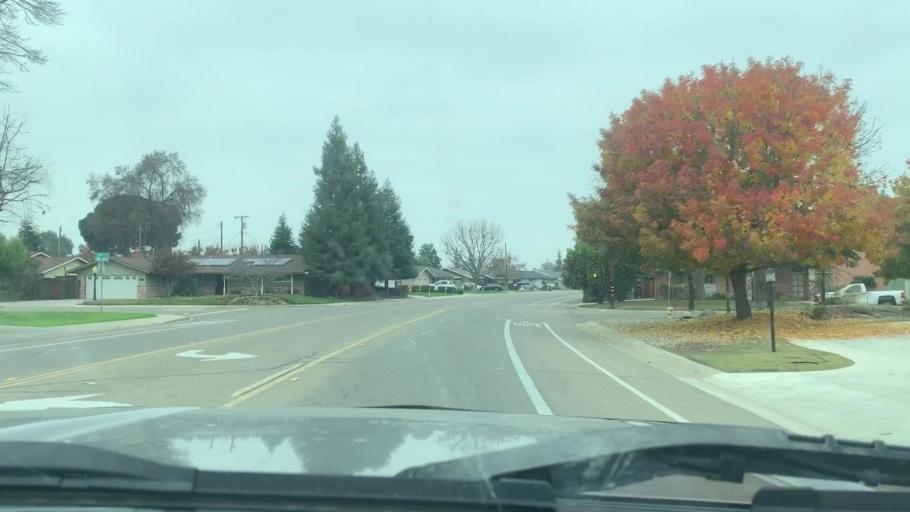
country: US
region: California
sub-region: Tulare County
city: Visalia
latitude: 36.3178
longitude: -119.3267
